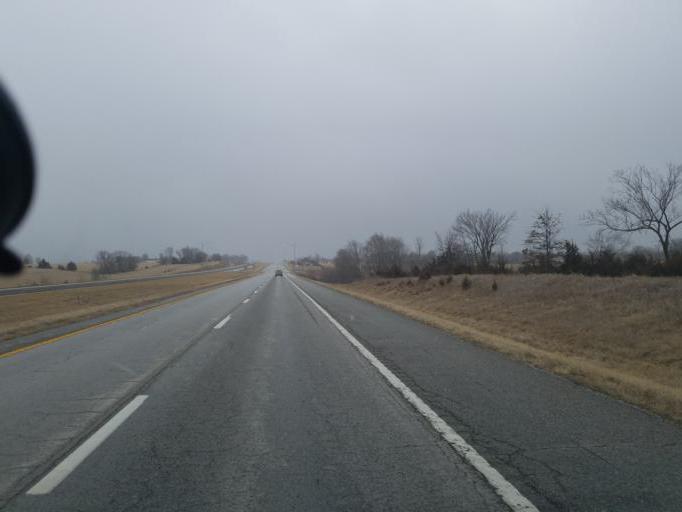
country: US
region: Missouri
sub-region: Macon County
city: La Plata
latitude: 39.9070
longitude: -92.4732
